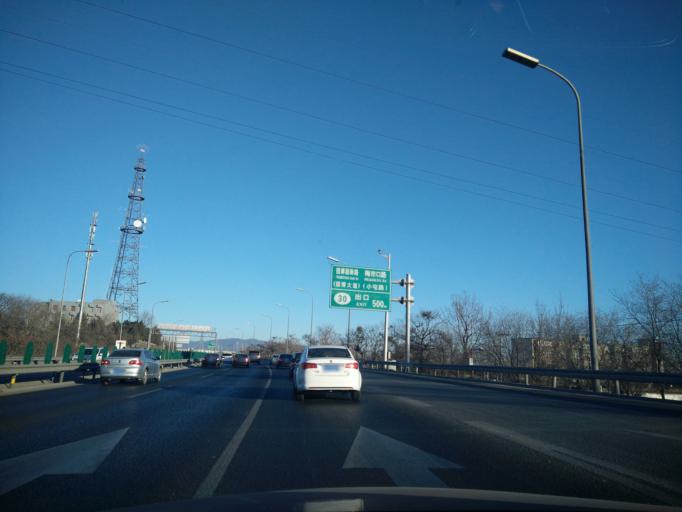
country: CN
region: Beijing
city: Lugu
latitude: 39.8562
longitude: 116.2140
